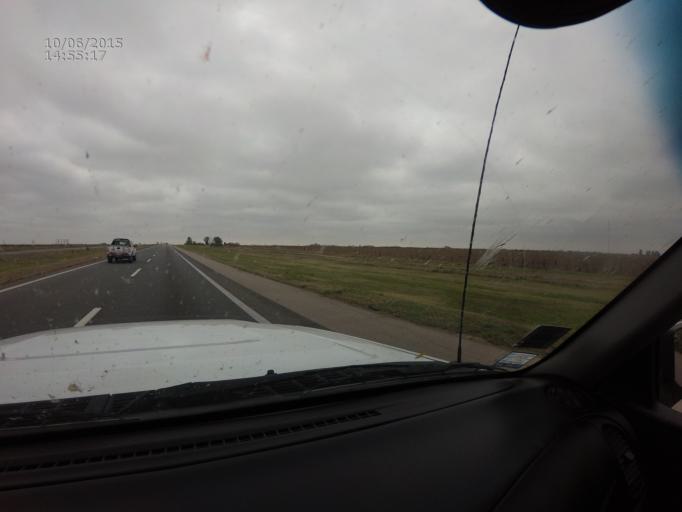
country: AR
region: Cordoba
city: Oncativo
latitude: -31.8417
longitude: -63.6955
